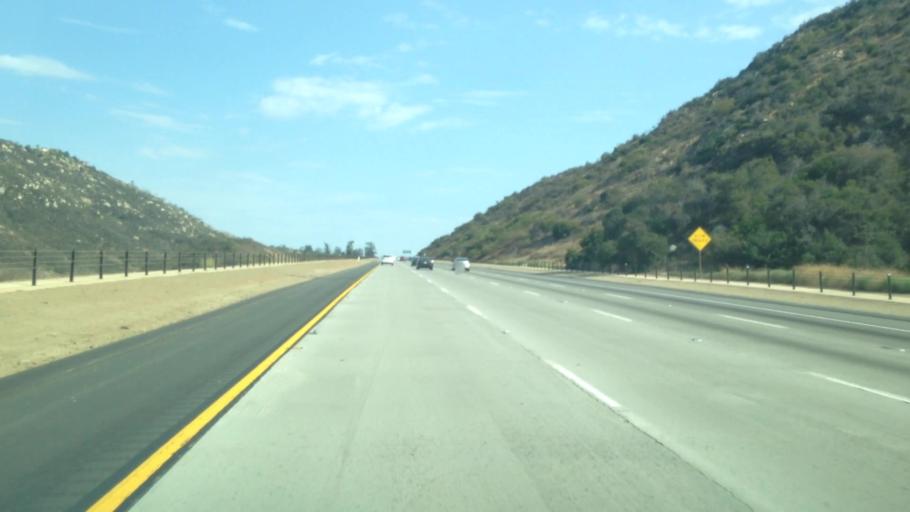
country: US
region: California
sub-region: San Diego County
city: Hidden Meadows
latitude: 33.2135
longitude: -117.1372
